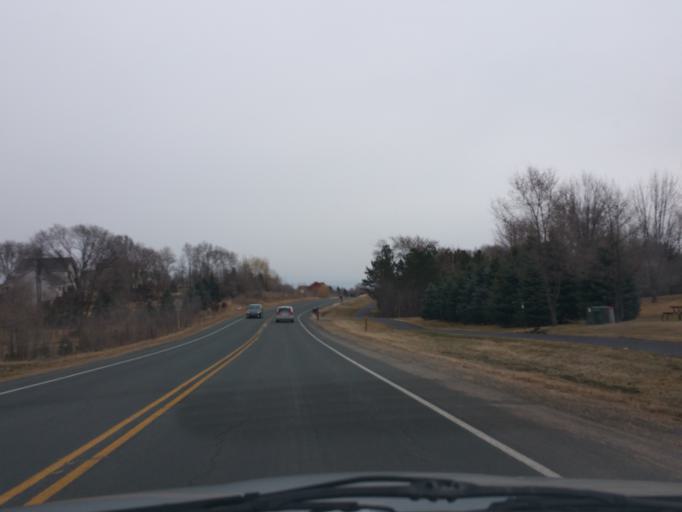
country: US
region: Wisconsin
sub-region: Saint Croix County
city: North Hudson
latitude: 44.9872
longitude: -92.7148
